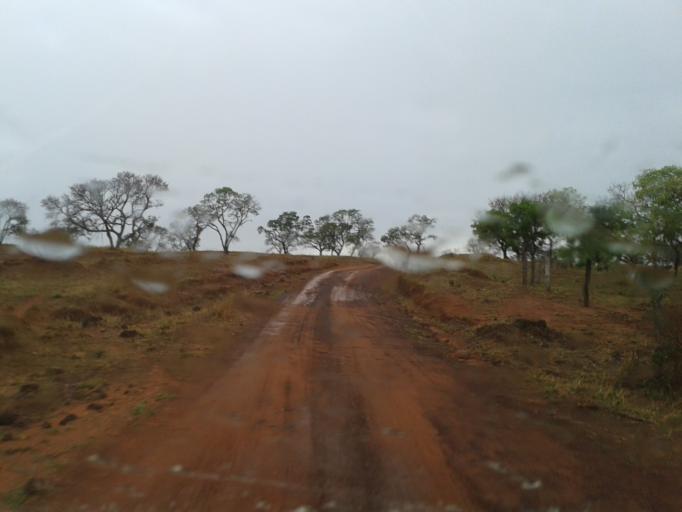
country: BR
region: Minas Gerais
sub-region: Campina Verde
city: Campina Verde
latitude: -19.3099
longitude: -49.5076
